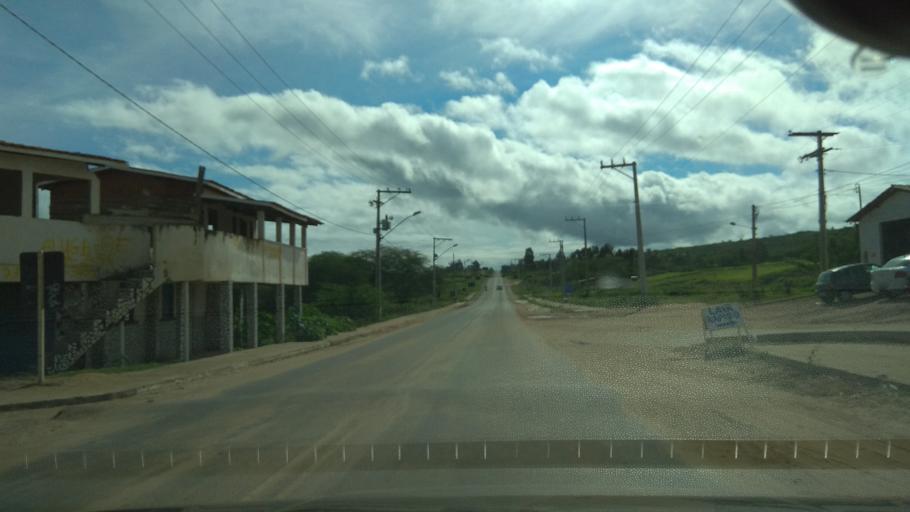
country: BR
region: Bahia
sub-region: Jaguaquara
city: Jaguaquara
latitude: -13.4470
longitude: -39.9372
